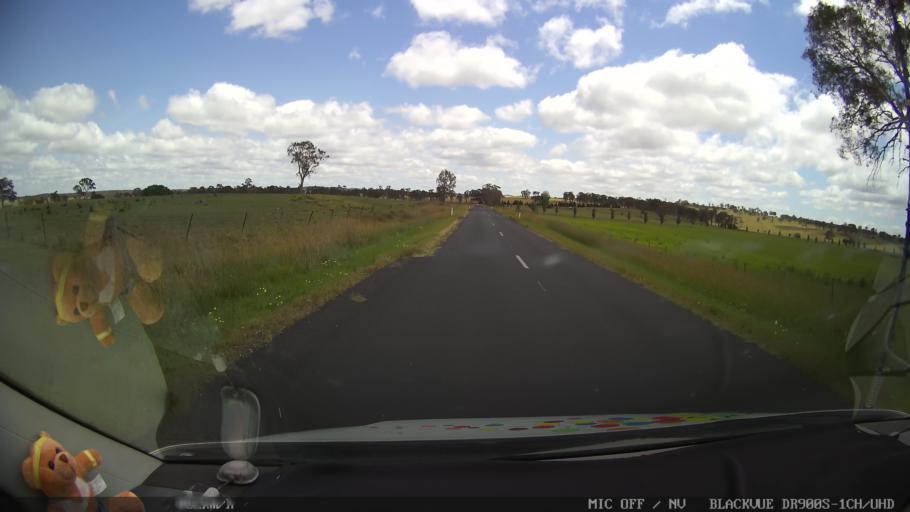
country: AU
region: New South Wales
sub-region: Glen Innes Severn
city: Glen Innes
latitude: -29.6568
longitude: 151.6929
